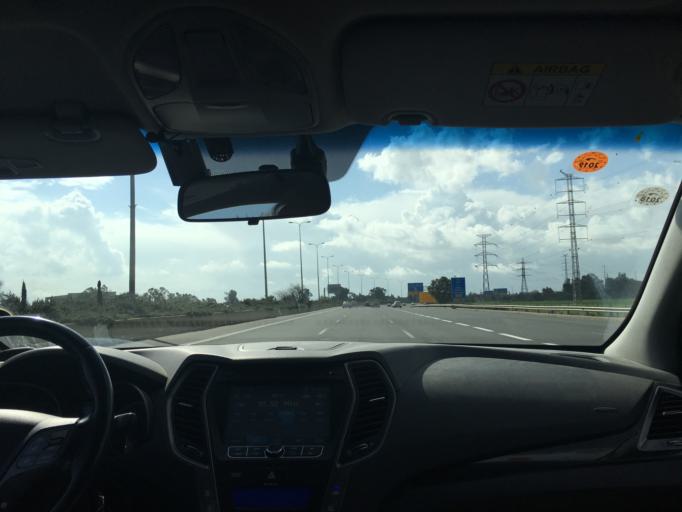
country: IL
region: Tel Aviv
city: Azor
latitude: 32.0327
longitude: 34.8290
